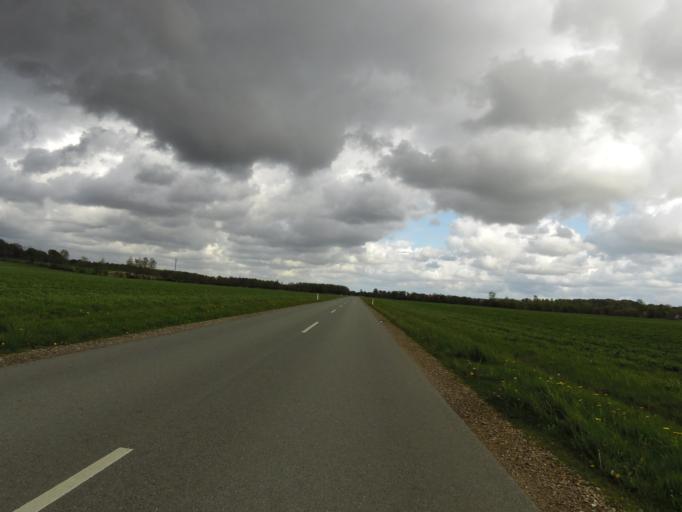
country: DK
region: South Denmark
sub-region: Haderslev Kommune
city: Gram
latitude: 55.3013
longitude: 9.0419
